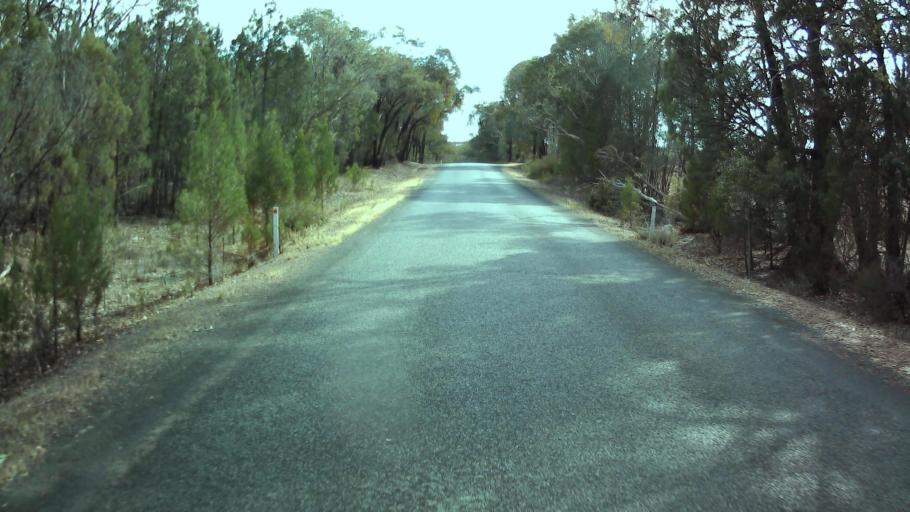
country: AU
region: New South Wales
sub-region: Weddin
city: Grenfell
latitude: -33.8922
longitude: 148.1909
